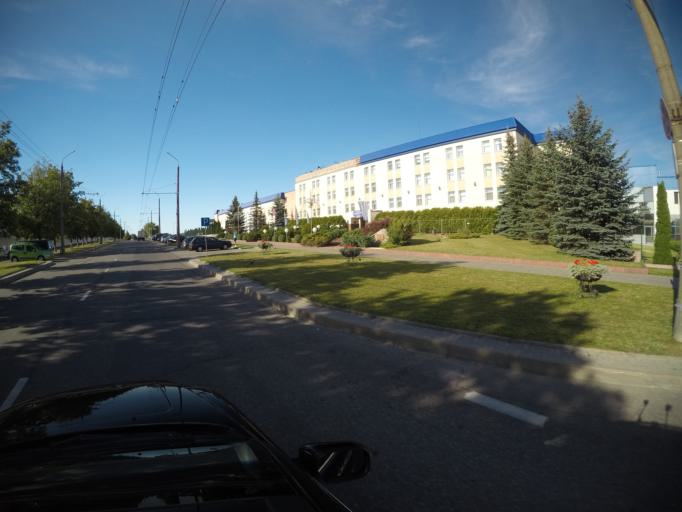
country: BY
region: Grodnenskaya
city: Hrodna
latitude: 53.7085
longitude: 23.8277
